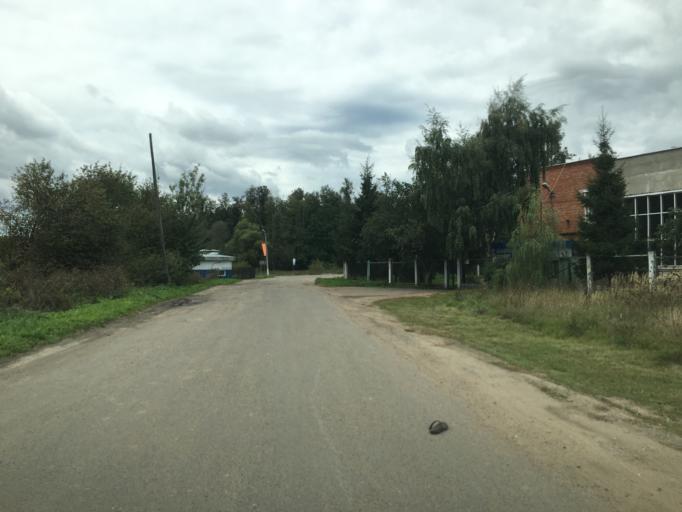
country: RU
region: Moskovskaya
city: Vatutinki
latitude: 55.4796
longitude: 37.4012
